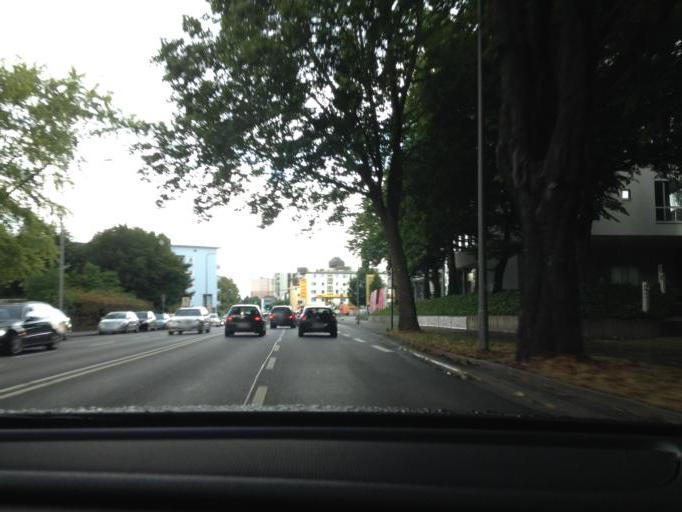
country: DE
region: Hesse
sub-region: Regierungsbezirk Darmstadt
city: Wiesbaden
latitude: 50.0716
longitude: 8.2263
